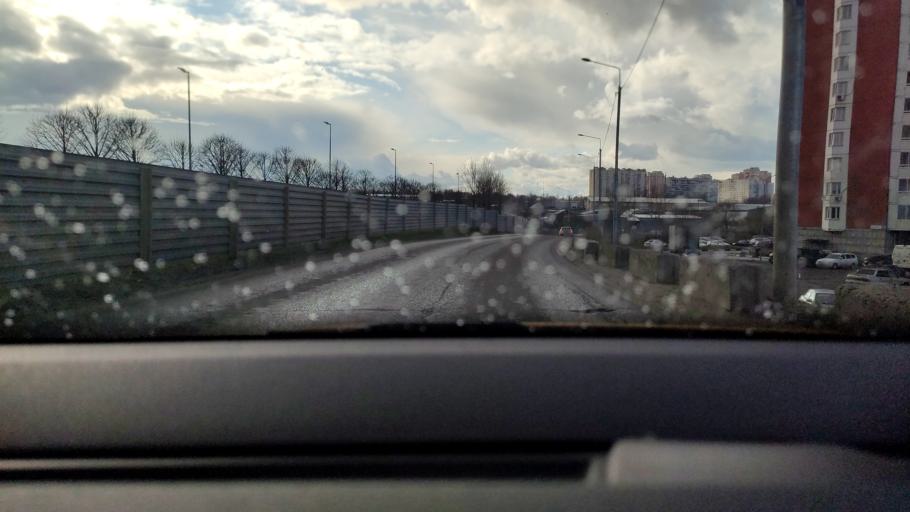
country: RU
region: Moskovskaya
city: Saltykovka
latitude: 55.7418
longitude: 37.9607
